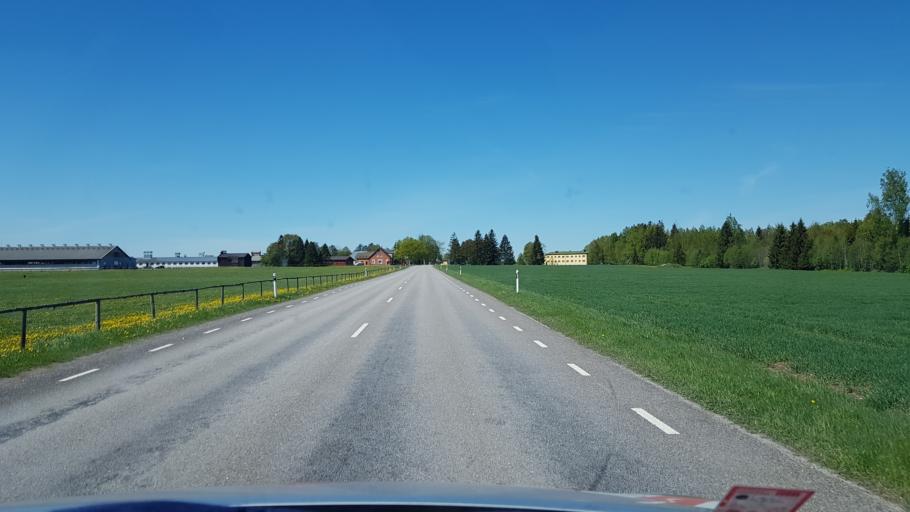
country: EE
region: Tartu
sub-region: Tartu linn
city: Tartu
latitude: 58.3809
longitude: 26.6285
